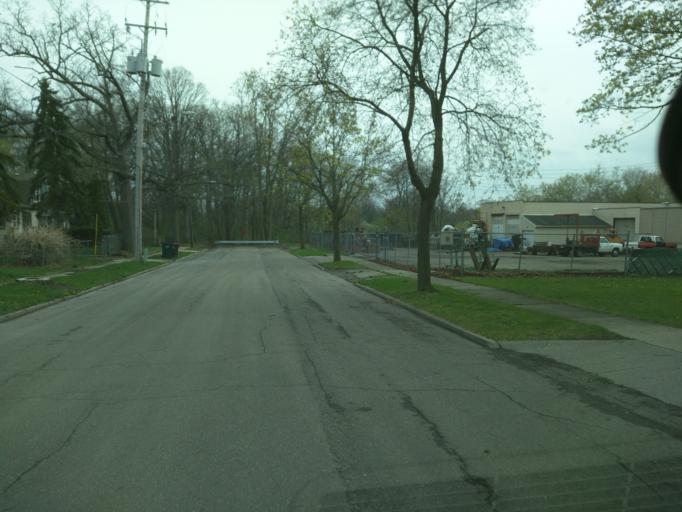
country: US
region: Michigan
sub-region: Ingham County
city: Lansing
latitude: 42.7201
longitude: -84.5331
